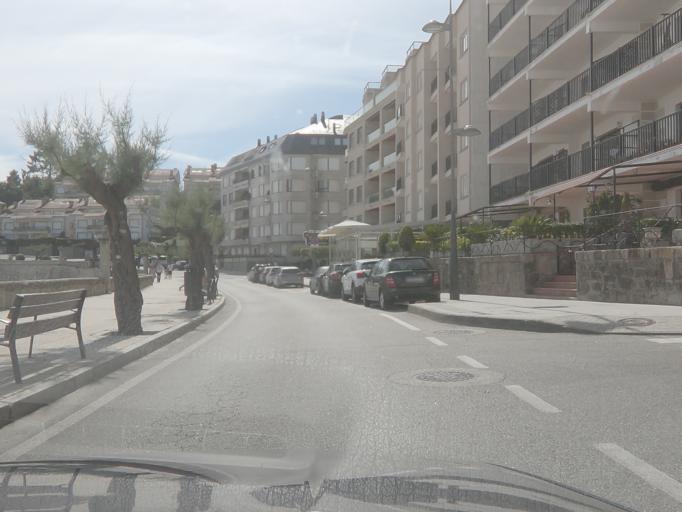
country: ES
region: Galicia
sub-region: Provincia de Pontevedra
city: Sanxenxo
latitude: 42.4014
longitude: -8.8151
